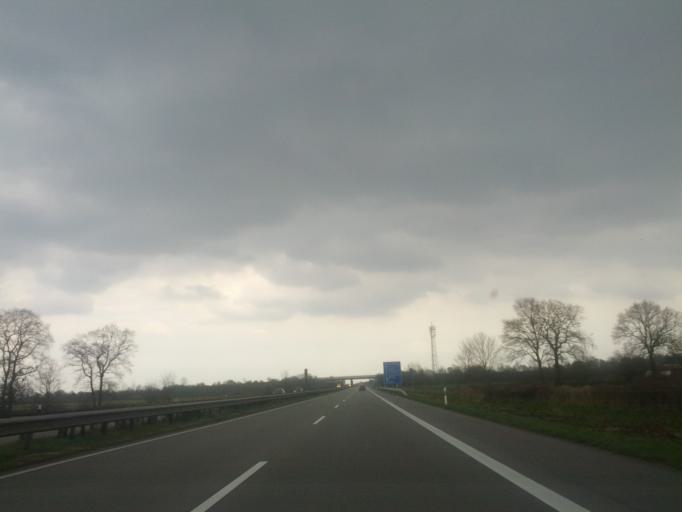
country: DE
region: Lower Saxony
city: Filsum
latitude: 53.2528
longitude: 7.6188
